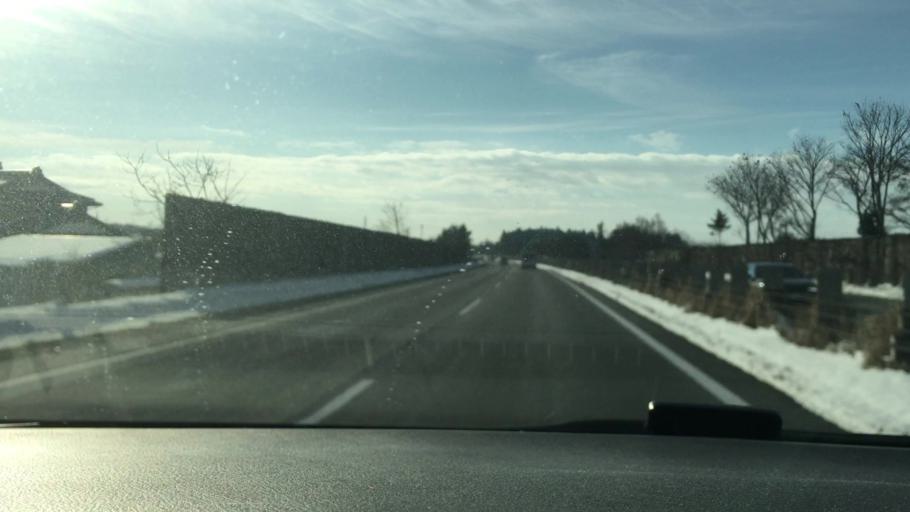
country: JP
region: Iwate
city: Hanamaki
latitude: 39.3539
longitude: 141.0893
